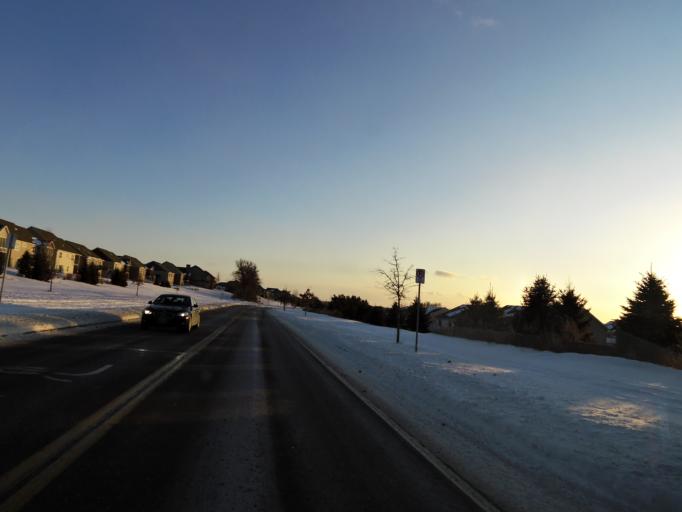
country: US
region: Minnesota
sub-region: Washington County
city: Lake Elmo
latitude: 44.9336
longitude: -92.8833
